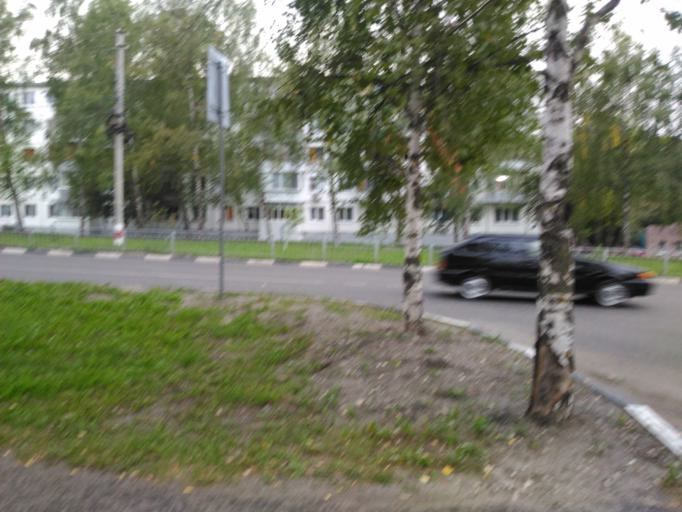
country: RU
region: Ulyanovsk
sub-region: Ulyanovskiy Rayon
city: Ulyanovsk
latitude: 54.2651
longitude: 48.3347
